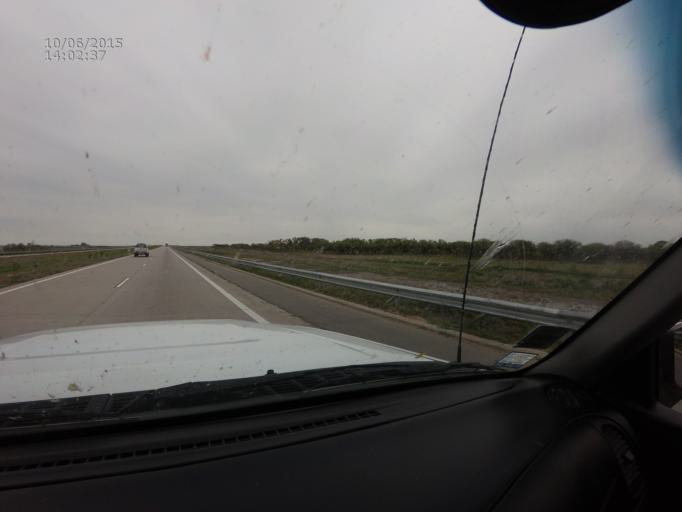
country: AR
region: Cordoba
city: Morrison
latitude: -32.5274
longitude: -62.9346
